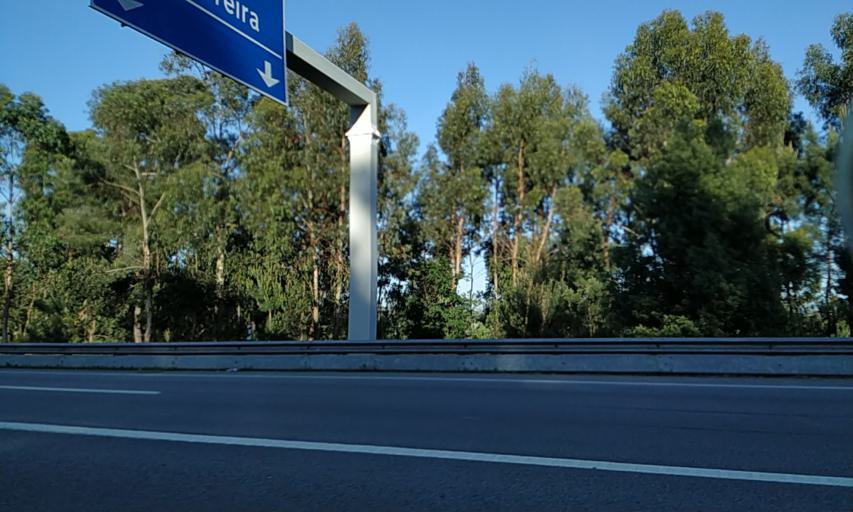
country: PT
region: Porto
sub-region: Valongo
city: Ermesinde
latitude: 41.2353
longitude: -8.5652
